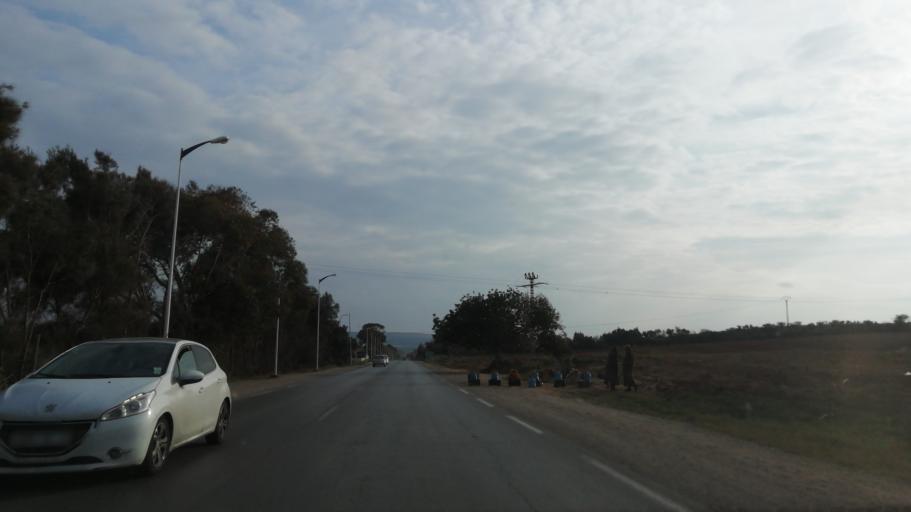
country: DZ
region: Mostaganem
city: Mostaganem
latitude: 35.8862
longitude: 0.0770
